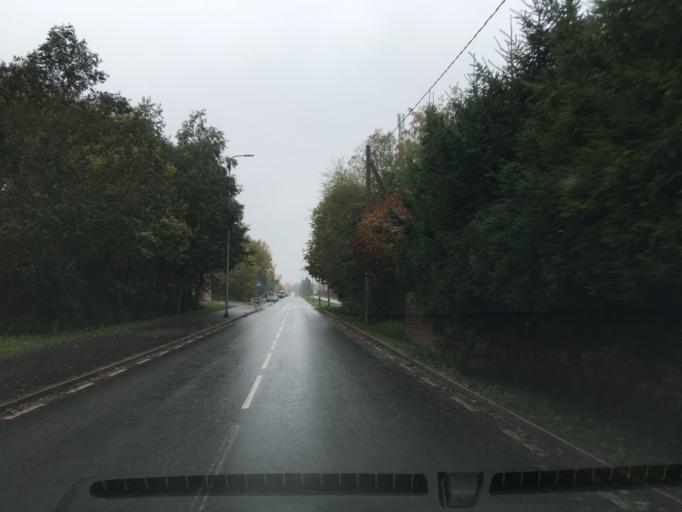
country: EE
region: Harju
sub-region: Tallinna linn
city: Kose
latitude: 59.4546
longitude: 24.8506
